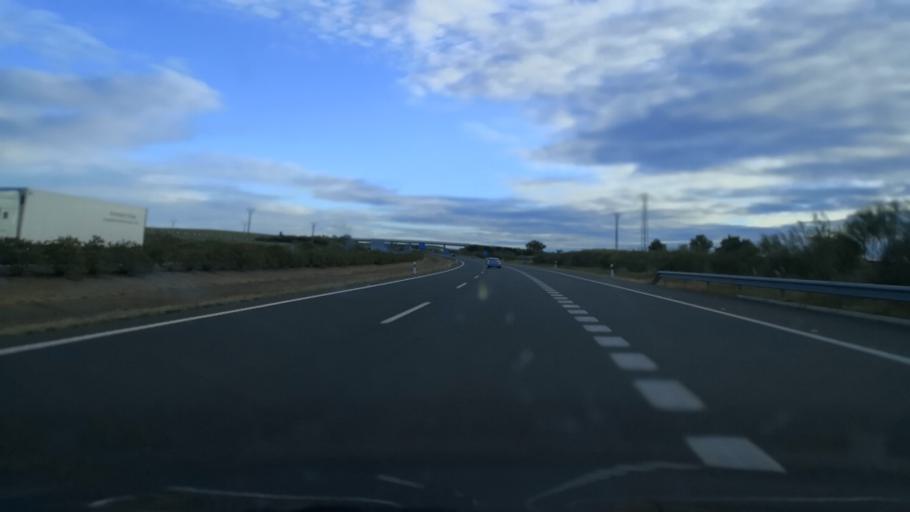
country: ES
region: Extremadura
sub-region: Provincia de Caceres
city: Casar de Caceres
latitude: 39.5522
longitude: -6.4027
